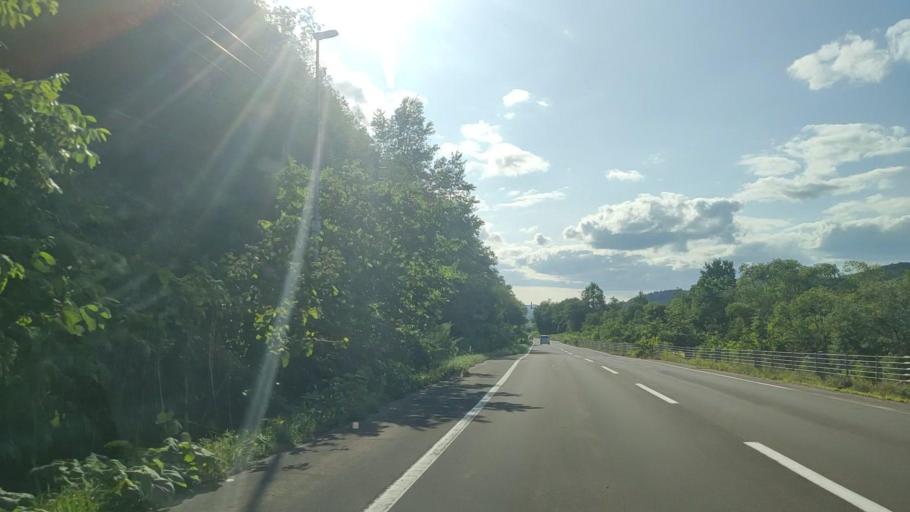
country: JP
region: Hokkaido
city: Nayoro
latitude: 44.7308
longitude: 142.0963
